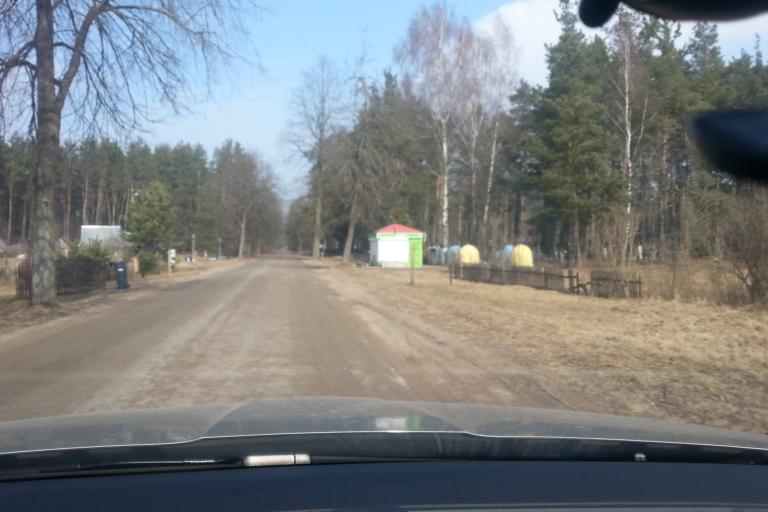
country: LT
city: Trakai
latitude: 54.5042
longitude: 24.9845
